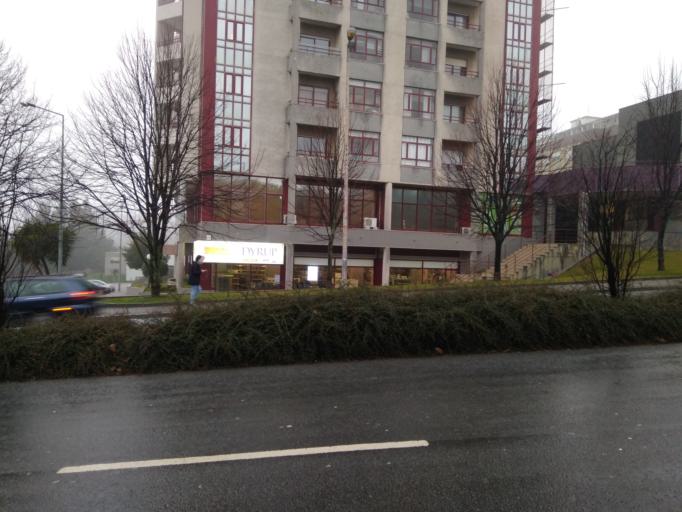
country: PT
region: Porto
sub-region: Vila Nova de Gaia
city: Vila Nova de Gaia
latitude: 41.1182
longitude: -8.6160
